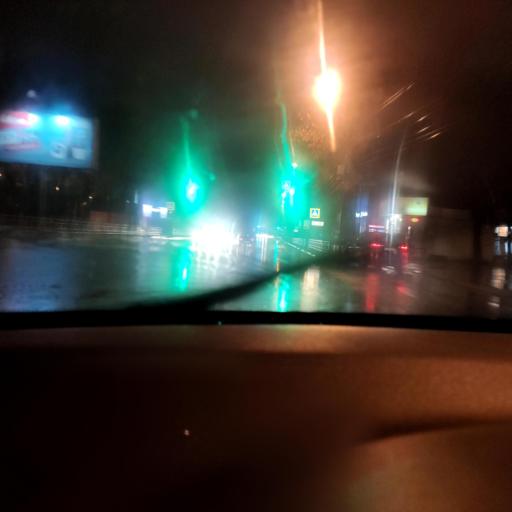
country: RU
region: Samara
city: Samara
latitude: 53.2164
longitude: 50.2091
